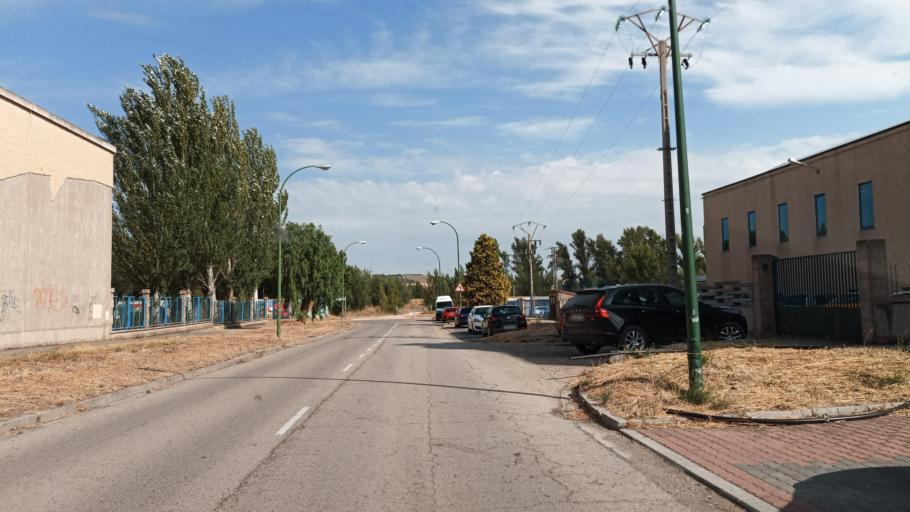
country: ES
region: Castille and Leon
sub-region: Provincia de Burgos
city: Burgos
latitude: 42.3630
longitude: -3.6473
